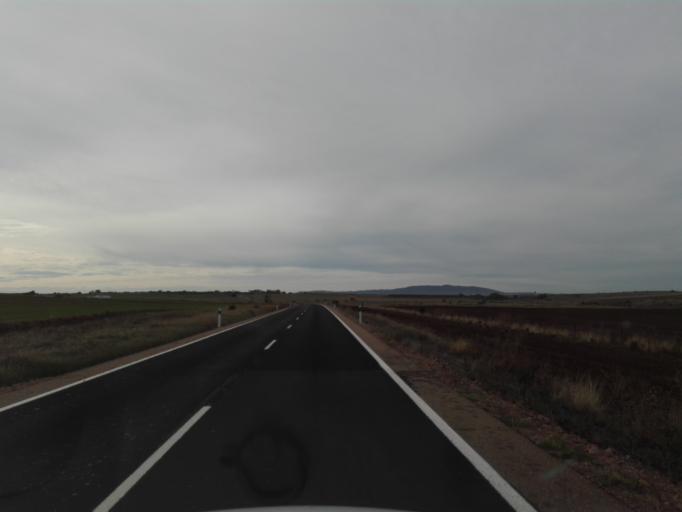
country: ES
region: Extremadura
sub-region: Provincia de Badajoz
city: Valencia de las Torres
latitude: 38.3334
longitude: -5.9643
